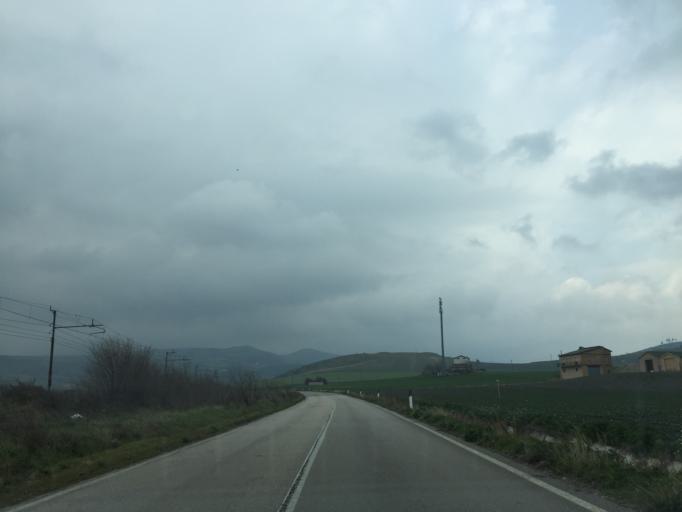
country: IT
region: Apulia
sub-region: Provincia di Foggia
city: Bovino
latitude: 41.2904
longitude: 15.3812
